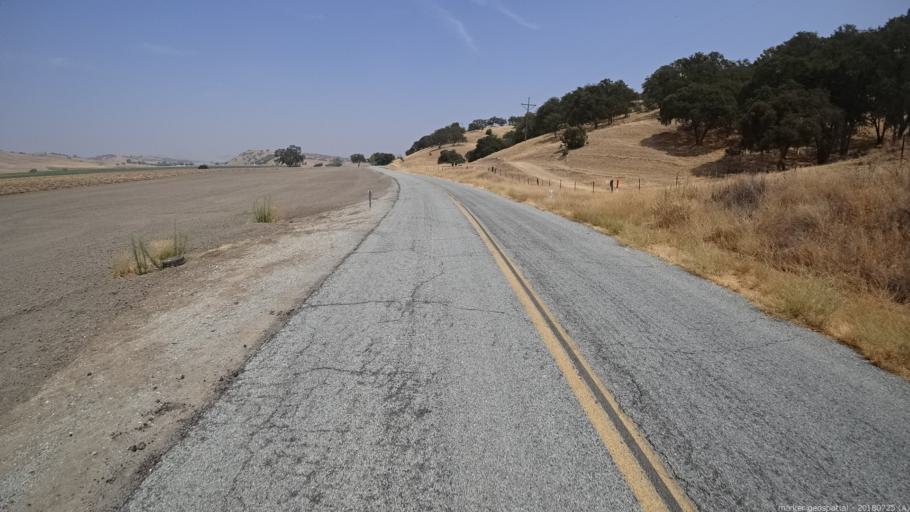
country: US
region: California
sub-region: San Luis Obispo County
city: San Miguel
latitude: 35.8166
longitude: -120.6621
